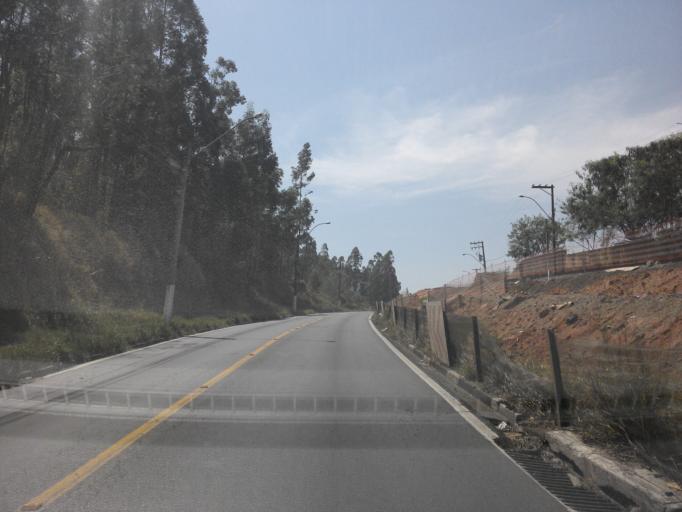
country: BR
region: Sao Paulo
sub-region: Hortolandia
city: Hortolandia
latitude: -22.9392
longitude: -47.1682
